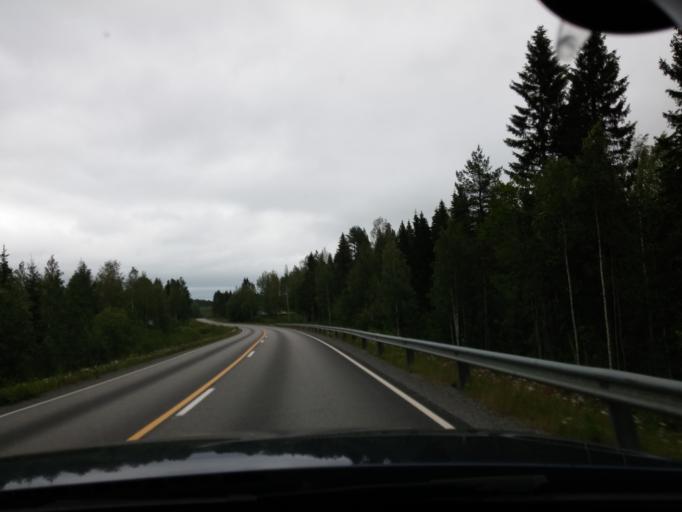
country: FI
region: Central Finland
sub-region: Saarijaervi-Viitasaari
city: Saarijaervi
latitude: 62.6792
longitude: 25.2280
